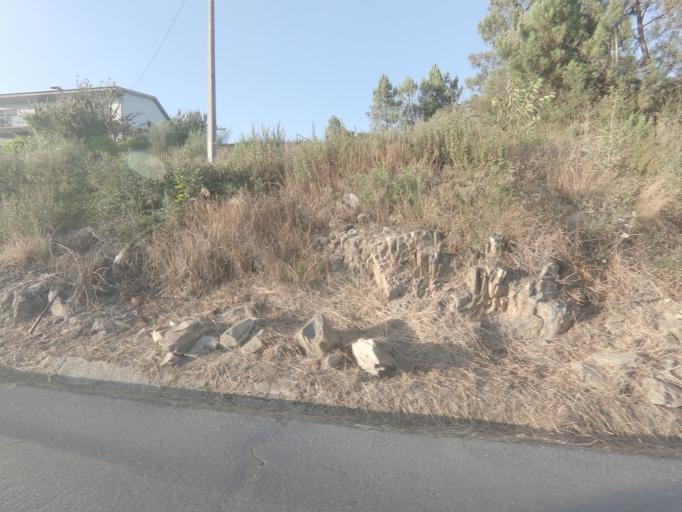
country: PT
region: Viseu
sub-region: Armamar
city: Armamar
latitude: 41.1915
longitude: -7.6858
